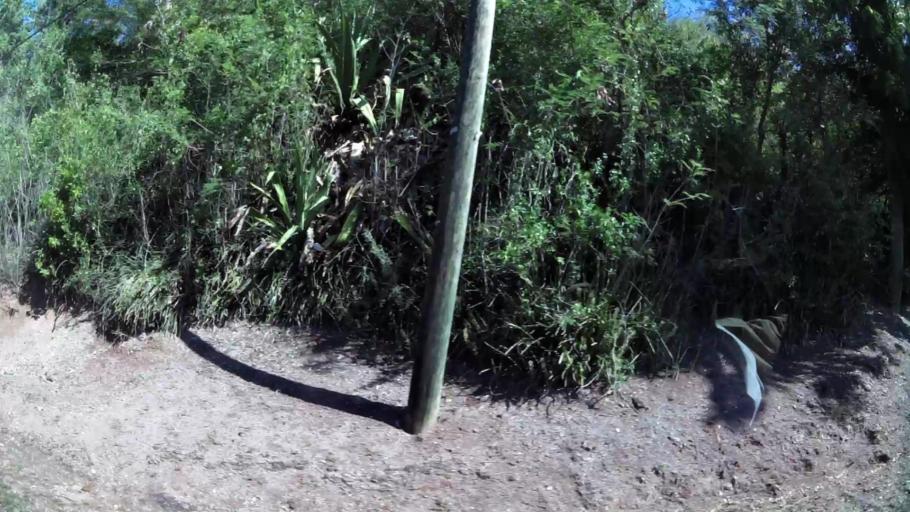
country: AG
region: Saint Paul
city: Falmouth
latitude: 17.0119
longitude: -61.7609
